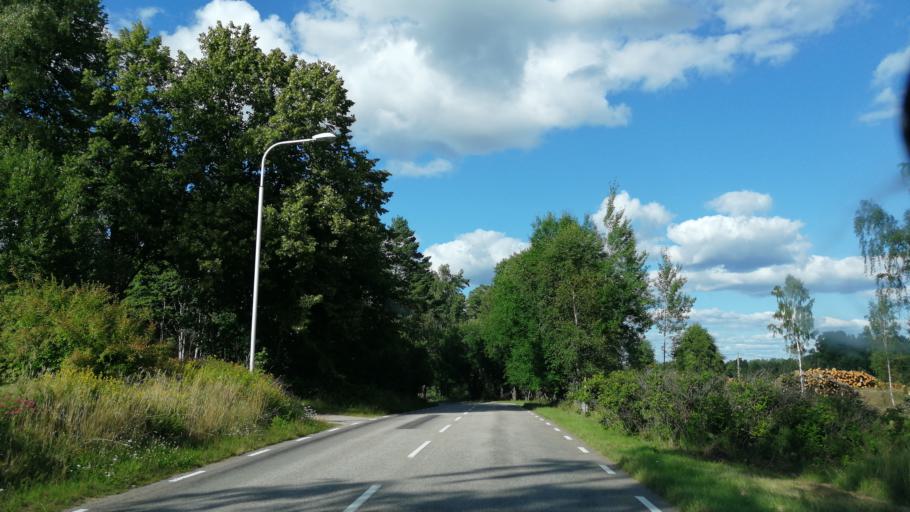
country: SE
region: Joenkoeping
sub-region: Varnamo Kommun
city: Bredaryd
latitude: 57.0920
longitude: 13.6864
